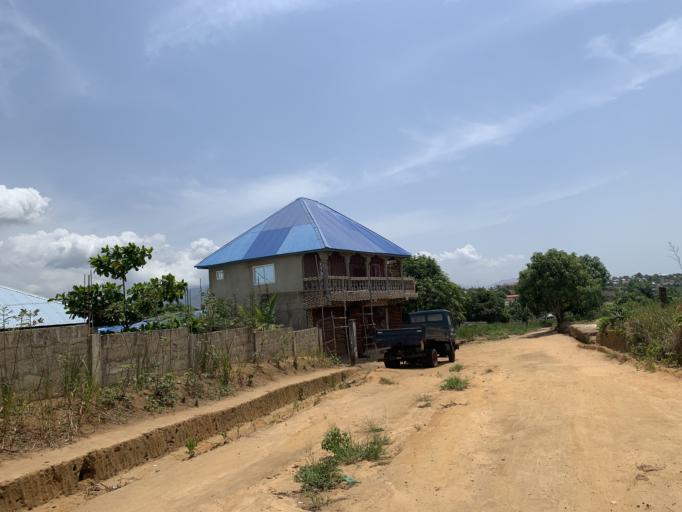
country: SL
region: Western Area
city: Waterloo
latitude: 8.3426
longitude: -13.0276
